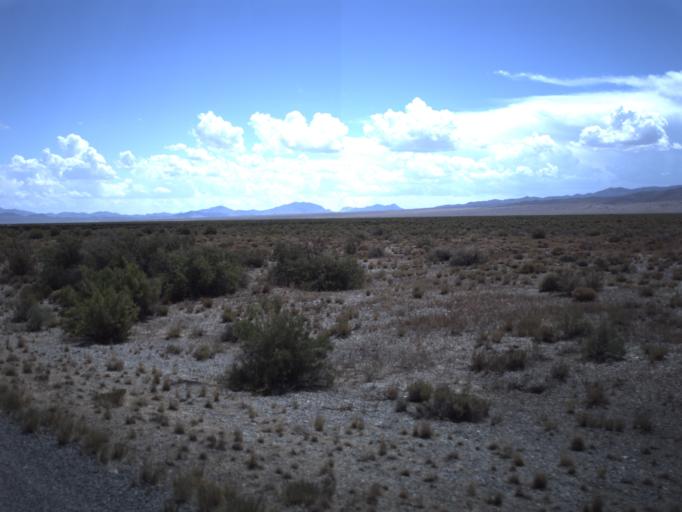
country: US
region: Nevada
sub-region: White Pine County
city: McGill
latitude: 39.0494
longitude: -113.9481
